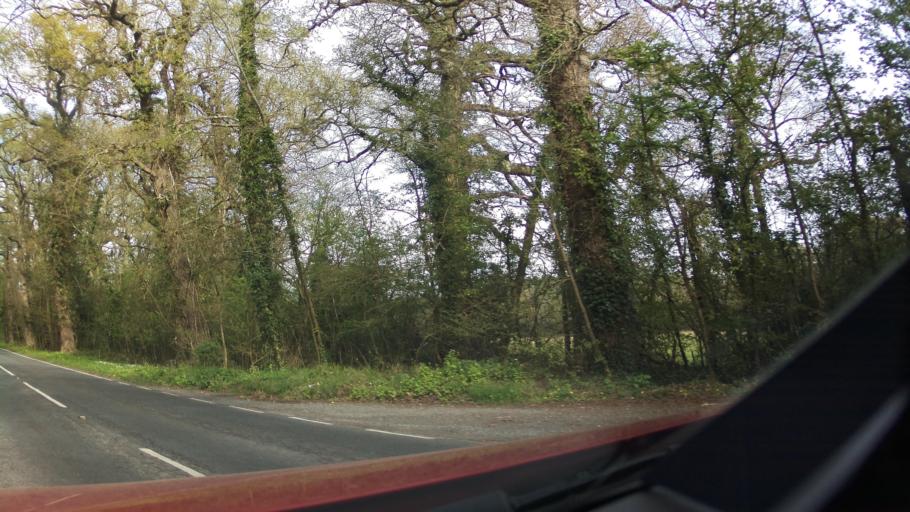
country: GB
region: England
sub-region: Hampshire
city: Chandlers Ford
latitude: 51.0121
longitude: -1.4031
